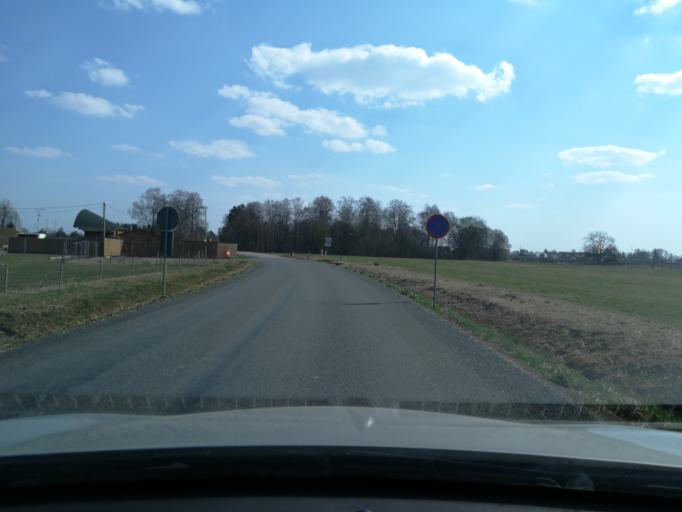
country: EE
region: Harju
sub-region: Saue linn
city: Saue
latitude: 59.3292
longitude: 24.5352
